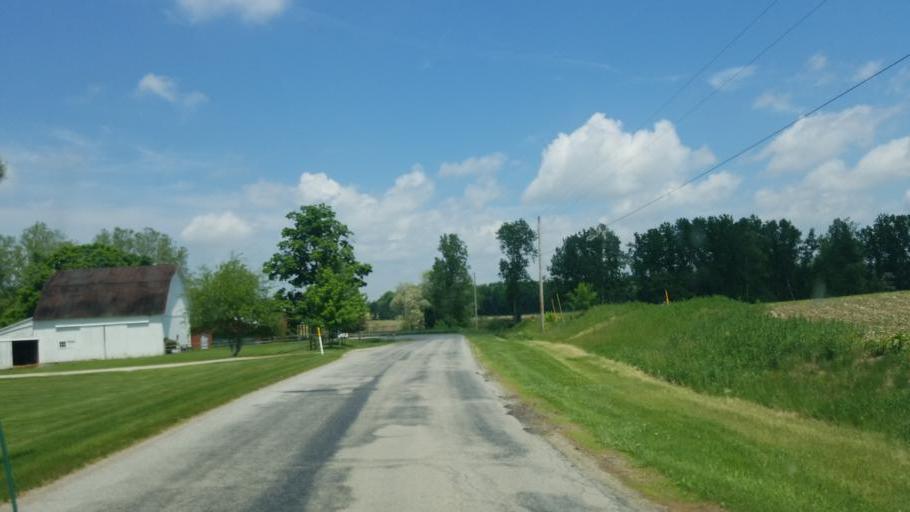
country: US
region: Ohio
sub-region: Ashland County
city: Ashland
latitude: 40.8329
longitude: -82.2507
